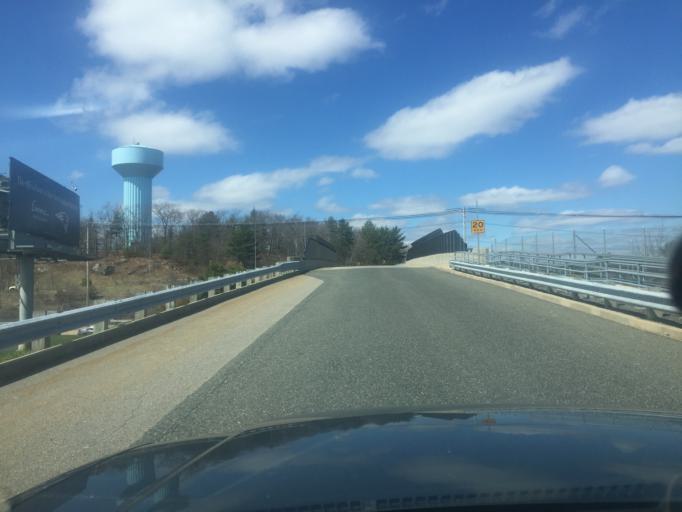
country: US
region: Massachusetts
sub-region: Norfolk County
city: Foxborough
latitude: 42.0887
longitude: -71.2715
